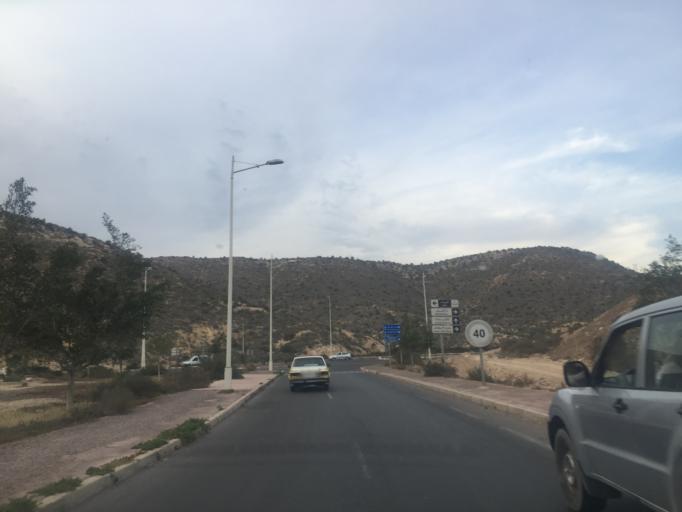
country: MA
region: Souss-Massa-Draa
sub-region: Agadir-Ida-ou-Tnan
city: Agadir
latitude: 30.4286
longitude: -9.6152
